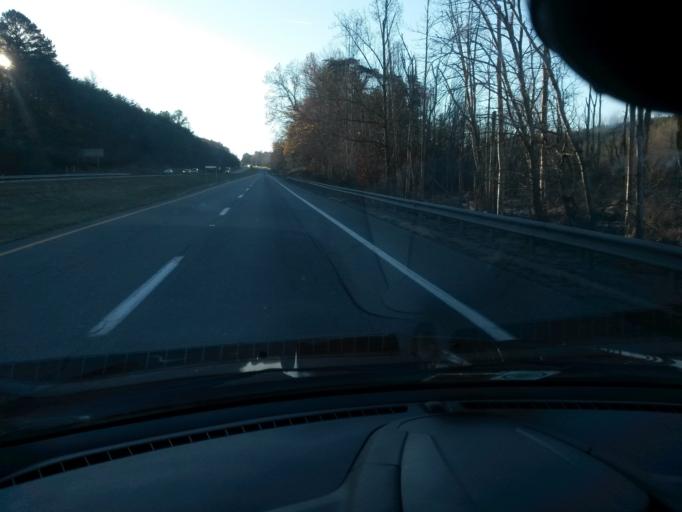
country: US
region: Virginia
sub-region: Henry County
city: Horse Pasture
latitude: 36.6582
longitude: -79.9252
